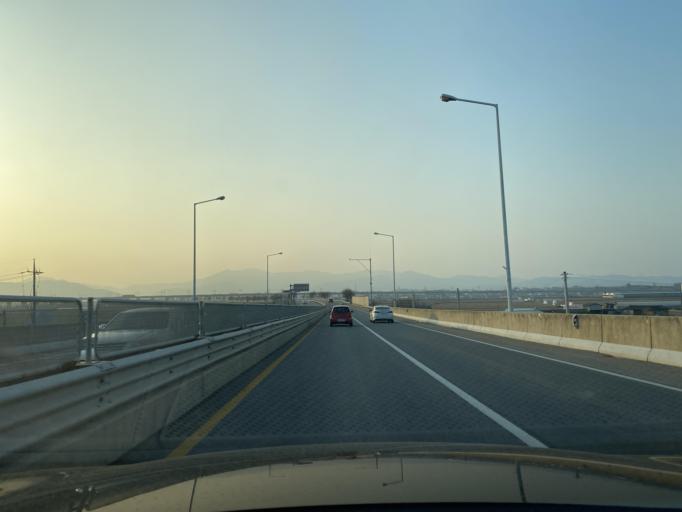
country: KR
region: Chungcheongnam-do
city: Yesan
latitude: 36.6917
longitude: 126.7356
